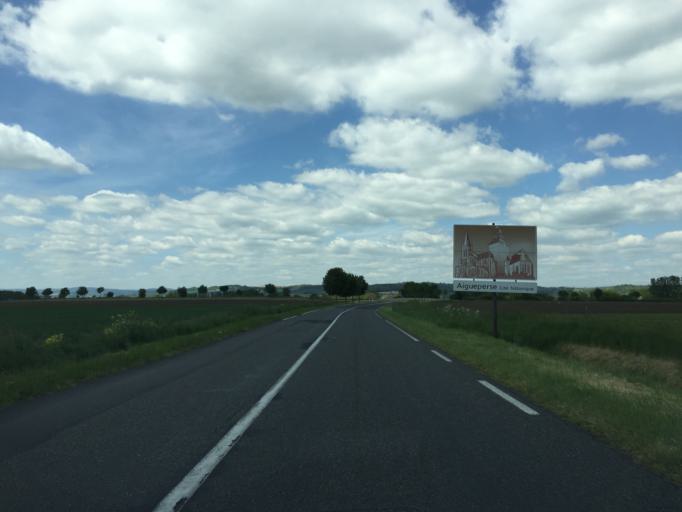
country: FR
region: Auvergne
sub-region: Departement du Puy-de-Dome
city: Aigueperse
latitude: 46.0231
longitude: 3.2210
